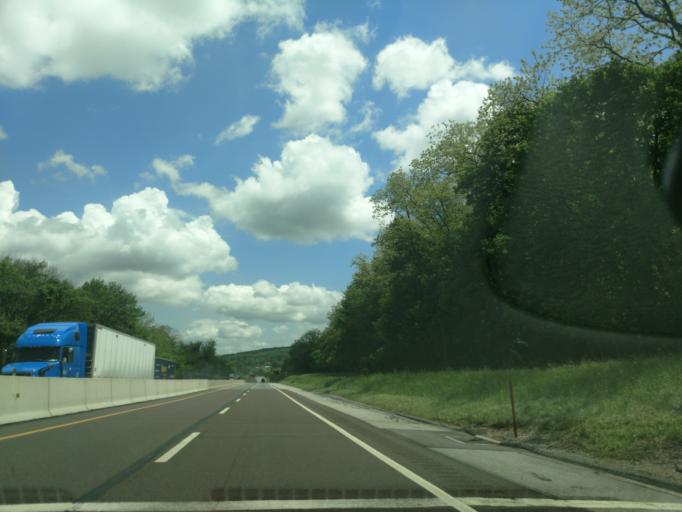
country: US
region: Pennsylvania
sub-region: Lancaster County
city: Denver
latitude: 40.2425
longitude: -76.1494
